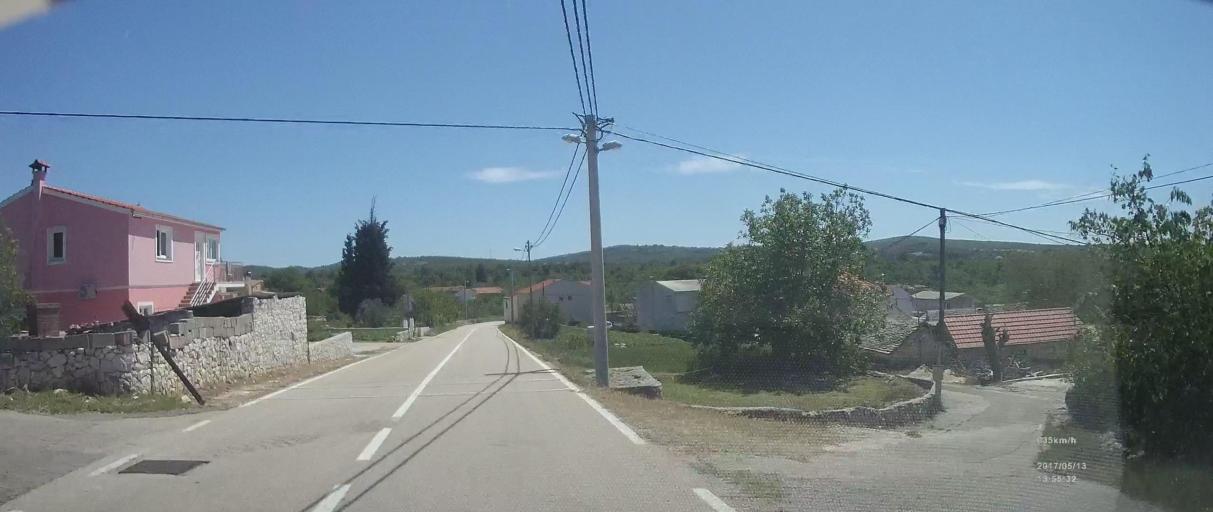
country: HR
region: Sibensko-Kniniska
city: Rogoznica
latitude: 43.5943
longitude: 16.0147
